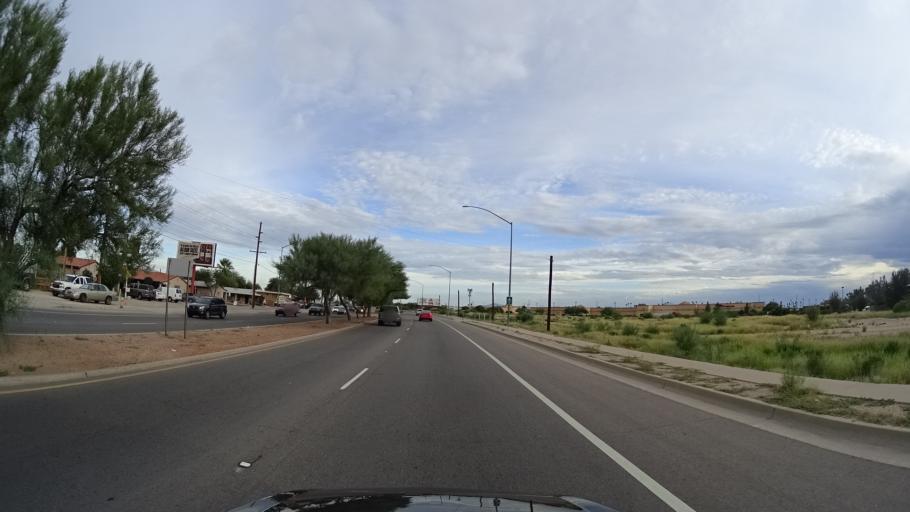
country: US
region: Arizona
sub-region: Pima County
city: South Tucson
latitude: 32.1678
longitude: -110.9424
